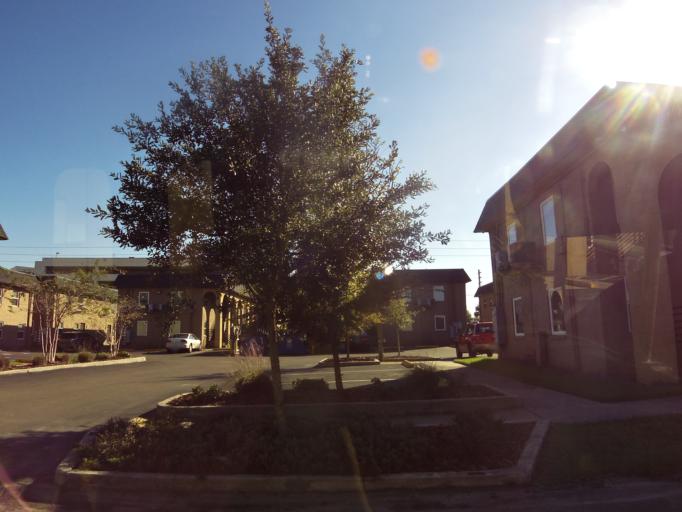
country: US
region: Florida
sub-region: Duval County
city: Jacksonville
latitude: 30.3511
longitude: -81.6659
